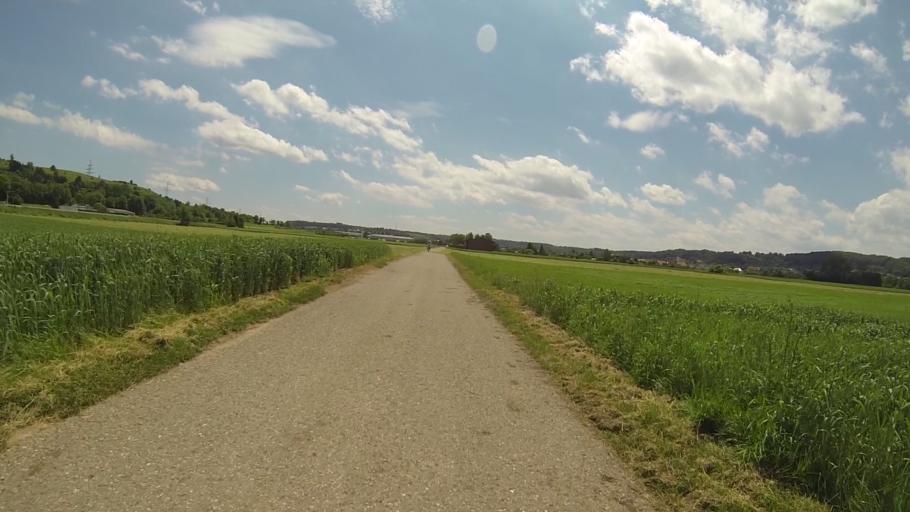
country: DE
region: Baden-Wuerttemberg
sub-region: Regierungsbezirk Stuttgart
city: Bolheim
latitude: 48.6393
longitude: 10.1625
